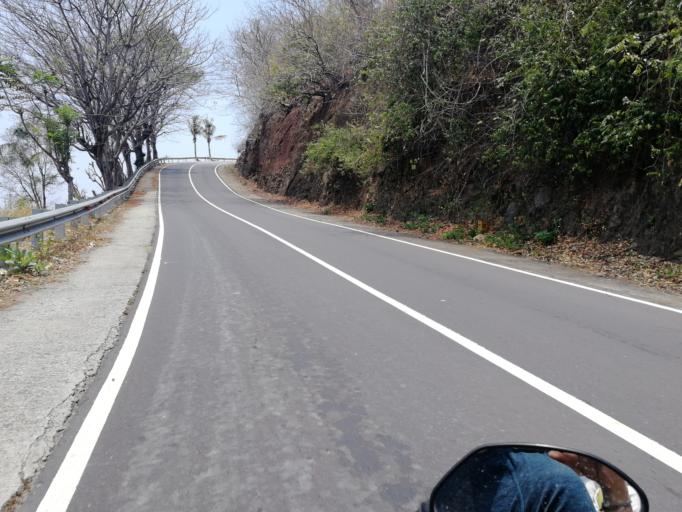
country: ID
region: West Nusa Tenggara
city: Karangsubagan
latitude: -8.4492
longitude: 116.0350
